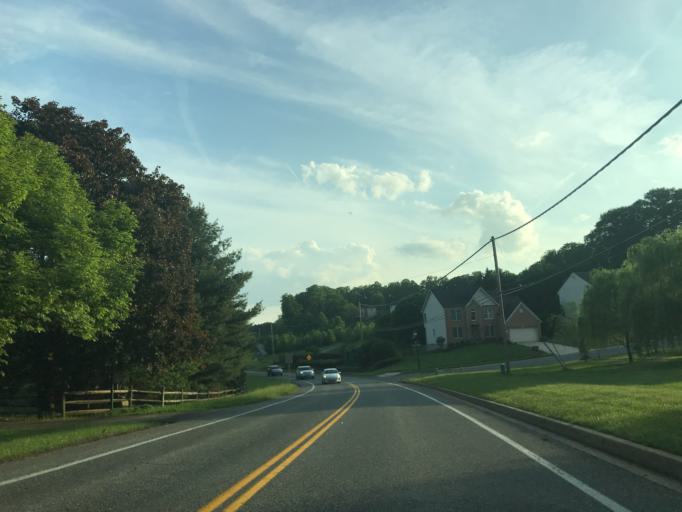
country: US
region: Maryland
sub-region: Harford County
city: South Bel Air
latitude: 39.5532
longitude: -76.3307
